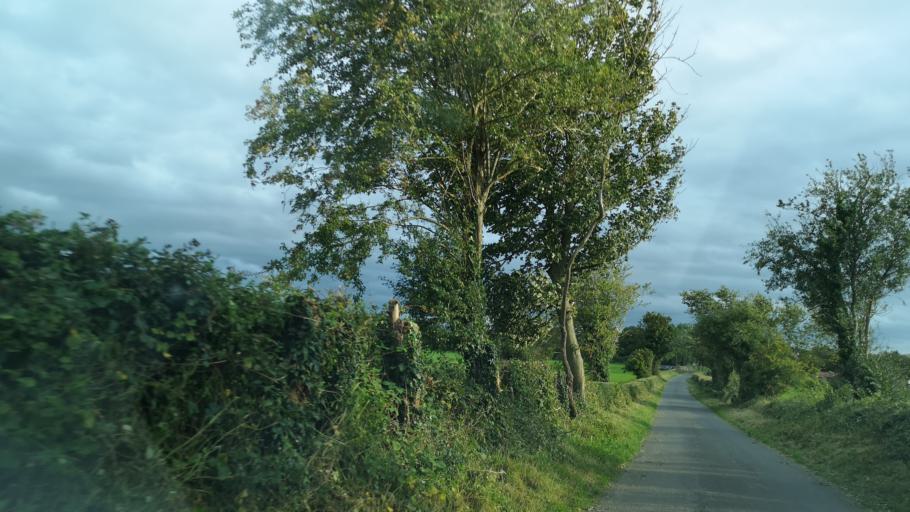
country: IE
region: Leinster
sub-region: Uibh Fhaili
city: Ferbane
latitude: 53.1833
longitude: -7.7269
